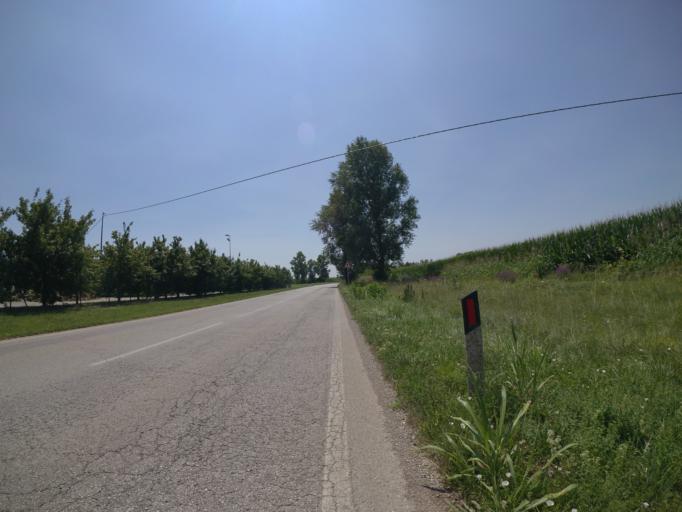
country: IT
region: Friuli Venezia Giulia
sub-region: Provincia di Udine
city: Lestizza
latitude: 45.9659
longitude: 13.1411
